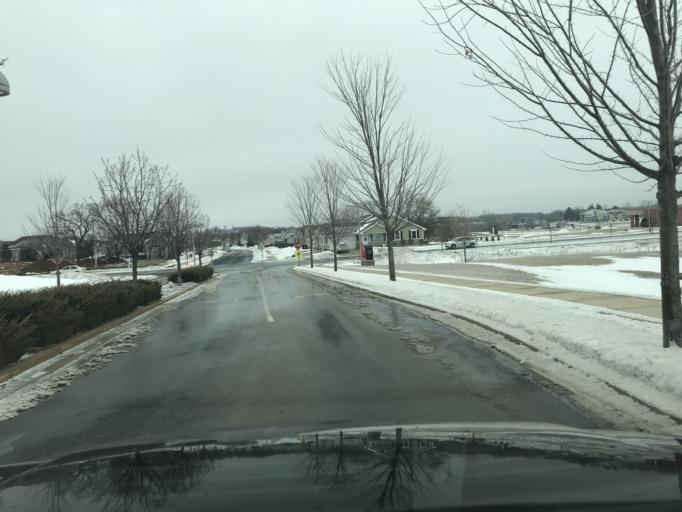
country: US
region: Wisconsin
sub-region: Dane County
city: Cottage Grove
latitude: 43.0909
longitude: -89.2213
